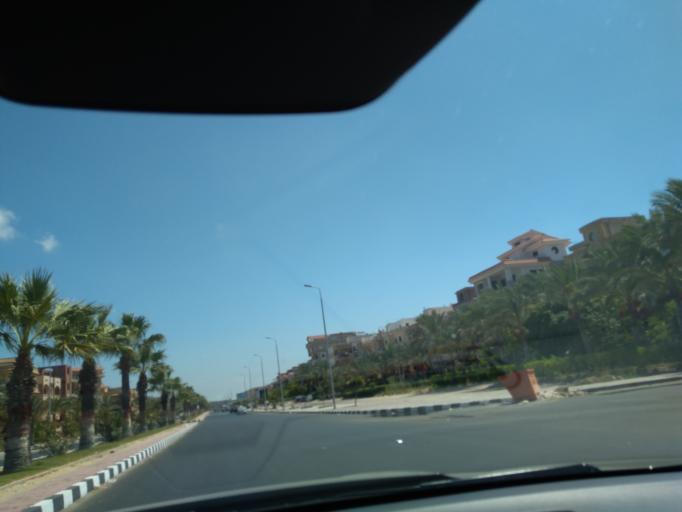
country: EG
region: Dumyat
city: Faraskur
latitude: 31.4312
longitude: 31.6734
